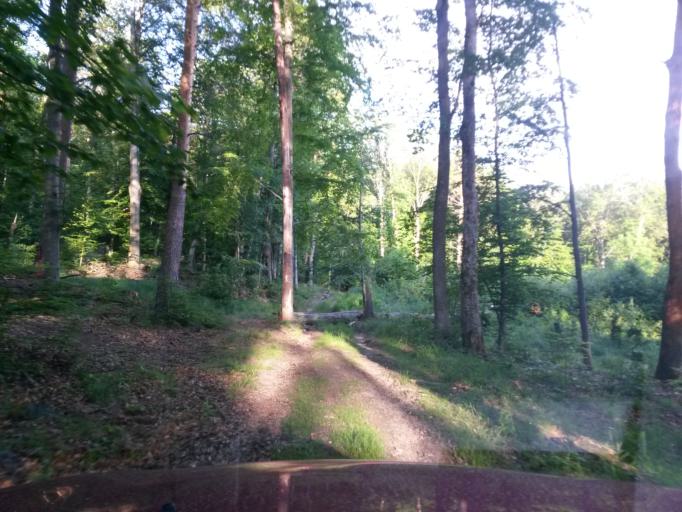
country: SK
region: Kosicky
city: Moldava nad Bodvou
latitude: 48.7328
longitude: 21.0443
